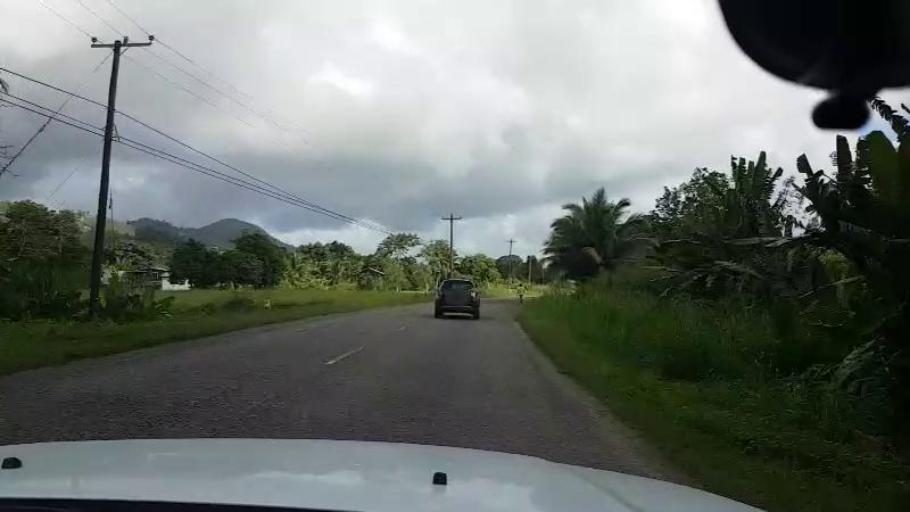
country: BZ
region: Stann Creek
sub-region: Dangriga
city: Dangriga
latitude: 17.0000
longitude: -88.4191
